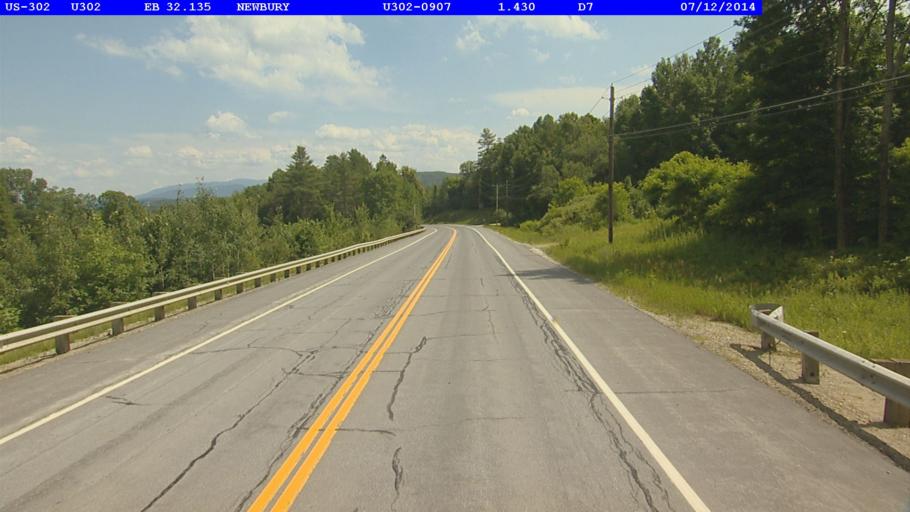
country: US
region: New Hampshire
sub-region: Grafton County
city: Woodsville
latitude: 44.1648
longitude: -72.0946
